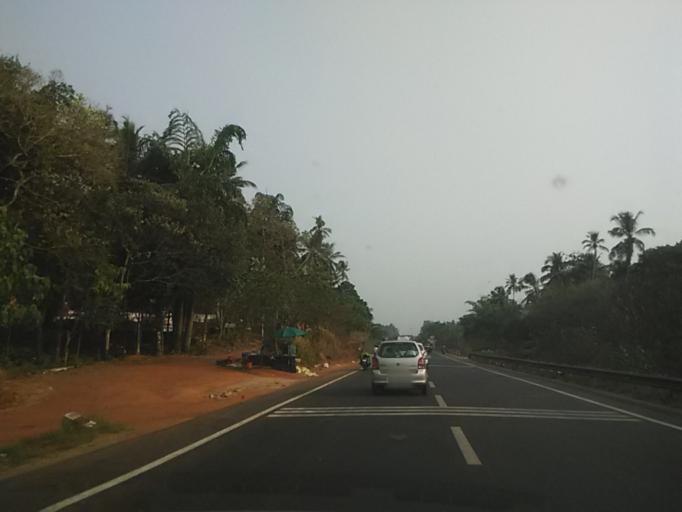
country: IN
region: Kerala
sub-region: Kozhikode
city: Kozhikode
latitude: 11.2948
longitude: 75.7974
